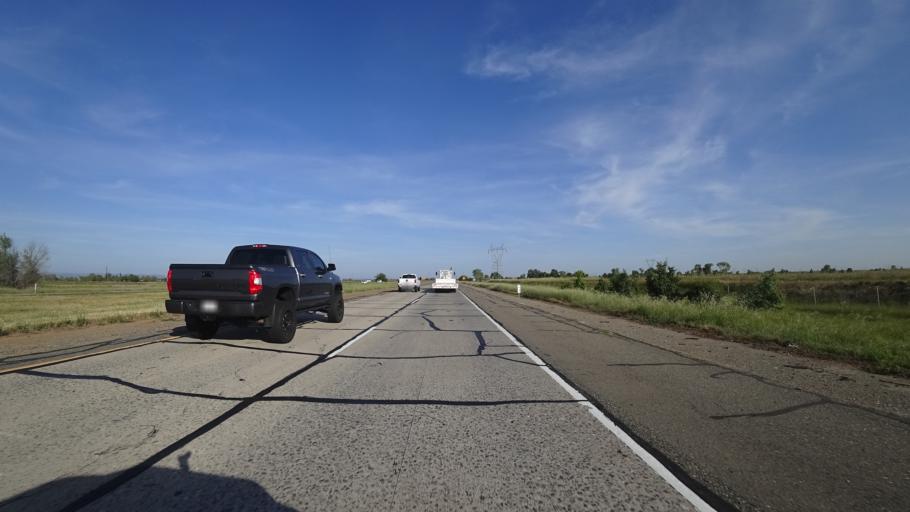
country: US
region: California
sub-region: Yuba County
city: Wheatland
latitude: 39.0460
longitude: -121.4869
